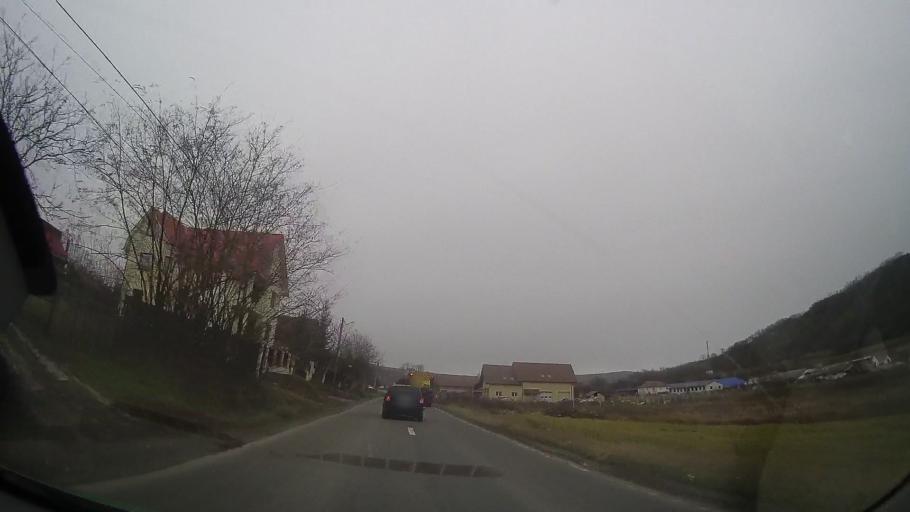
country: RO
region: Mures
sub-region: Comuna Ceausu de Campie
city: Ceausu de Campie
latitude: 46.6343
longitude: 24.5177
